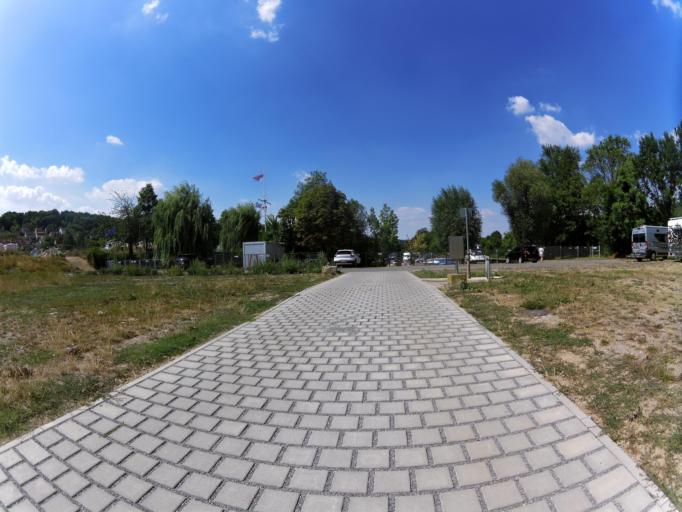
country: DE
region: Bavaria
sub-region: Regierungsbezirk Unterfranken
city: Ochsenfurt
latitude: 49.6670
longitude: 10.0596
